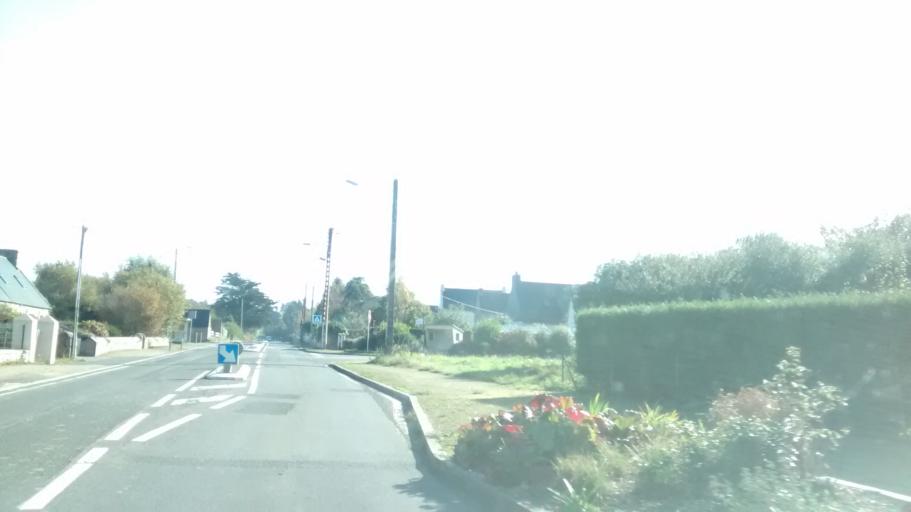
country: FR
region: Brittany
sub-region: Departement des Cotes-d'Armor
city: Trebeurden
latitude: 48.7651
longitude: -3.5481
